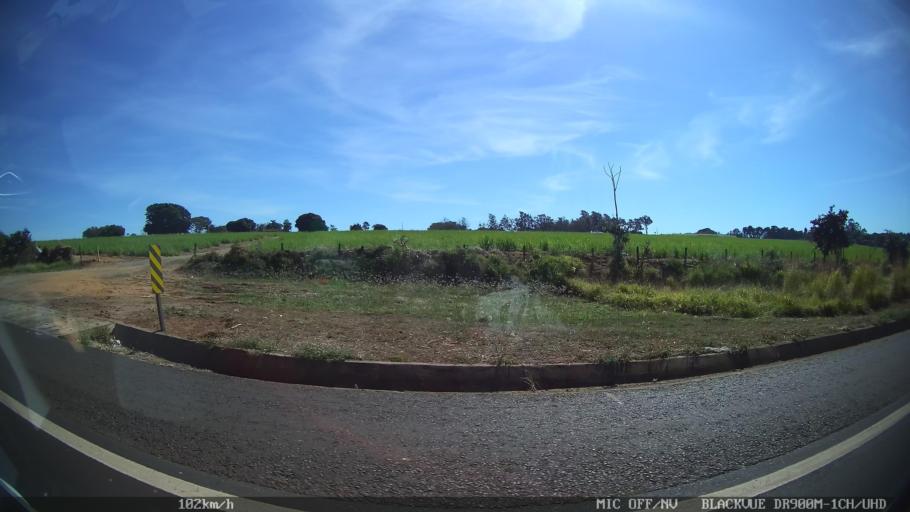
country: BR
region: Sao Paulo
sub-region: Franca
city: Franca
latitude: -20.5525
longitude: -47.4896
